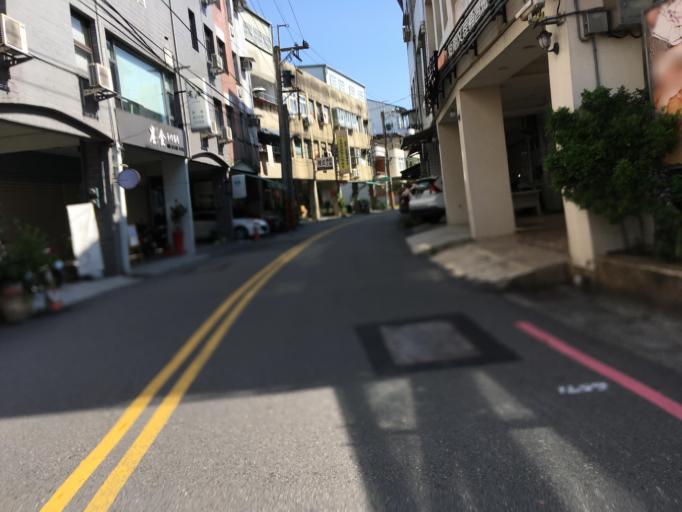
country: TW
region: Taiwan
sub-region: Yilan
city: Yilan
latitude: 24.6824
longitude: 121.7637
